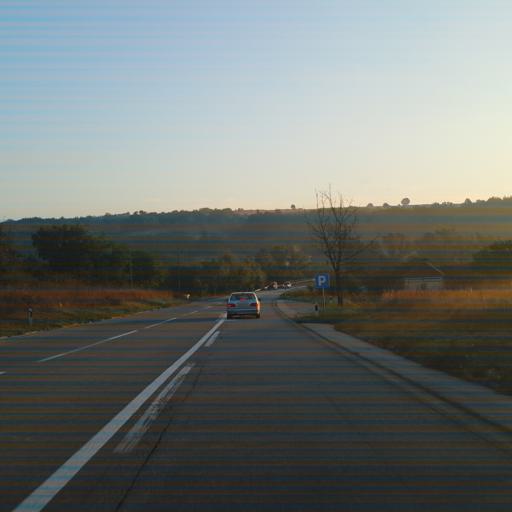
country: RS
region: Central Serbia
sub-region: Zajecarski Okrug
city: Zajecar
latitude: 44.0280
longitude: 22.3268
